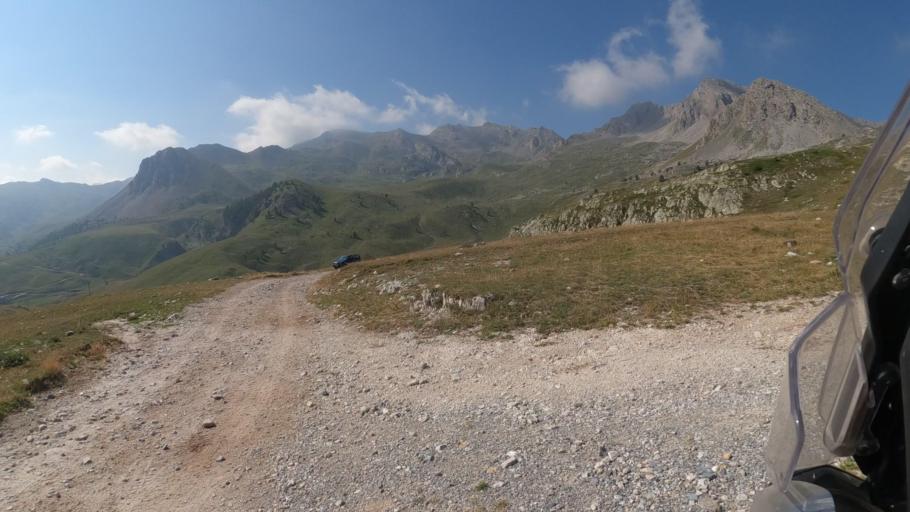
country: IT
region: Piedmont
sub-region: Provincia di Cuneo
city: Pietraporzio
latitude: 44.4039
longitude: 7.0304
